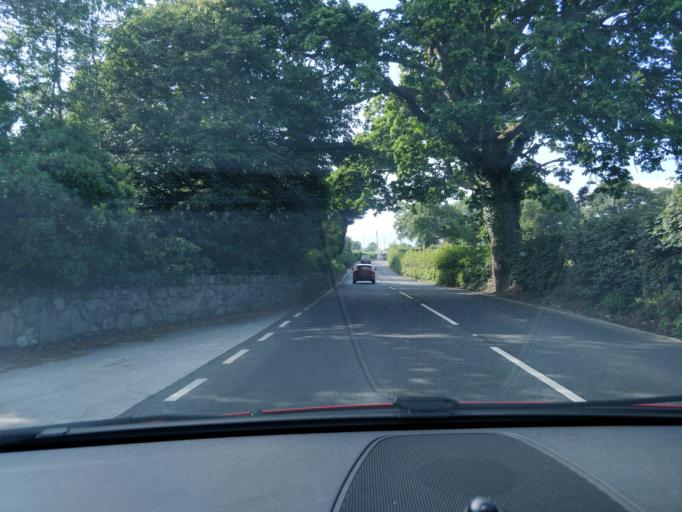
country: GB
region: Wales
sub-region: Conwy
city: Llansantffraid Glan Conwy
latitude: 53.2478
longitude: -3.7973
